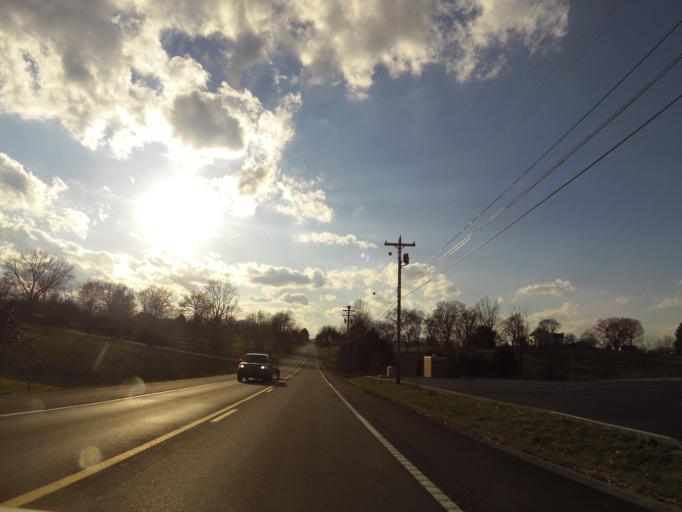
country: US
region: Tennessee
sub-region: Smith County
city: Carthage
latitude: 36.2585
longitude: -85.9725
